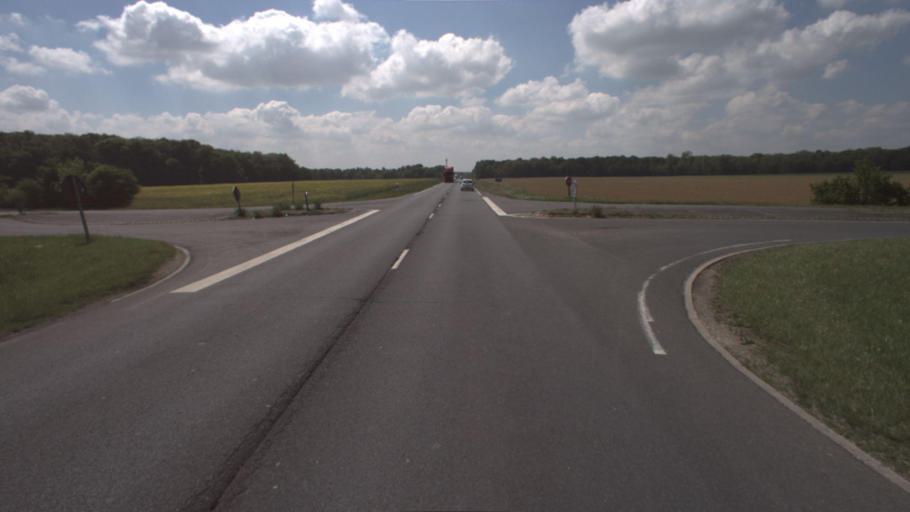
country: FR
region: Ile-de-France
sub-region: Departement de Seine-et-Marne
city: Chaumes-en-Brie
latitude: 48.6755
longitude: 2.8133
